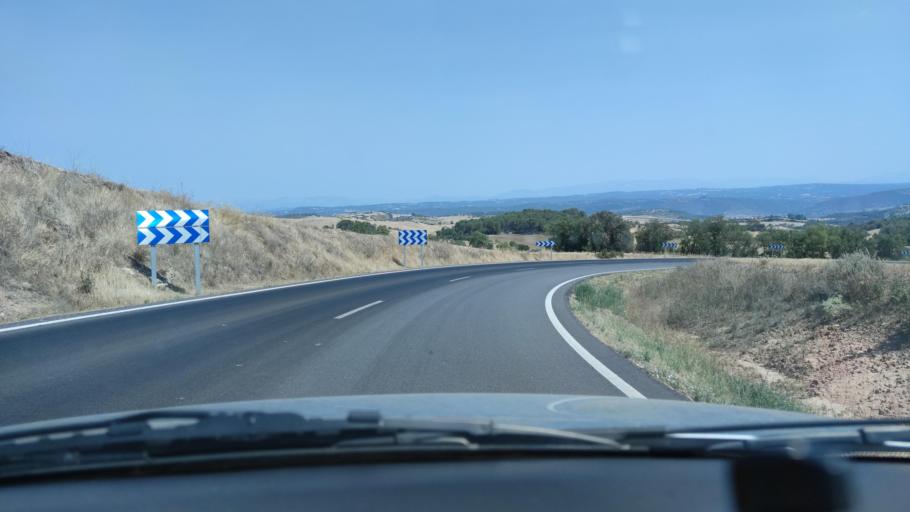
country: ES
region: Catalonia
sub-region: Provincia de Lleida
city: Ivorra
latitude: 41.7661
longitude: 1.3789
